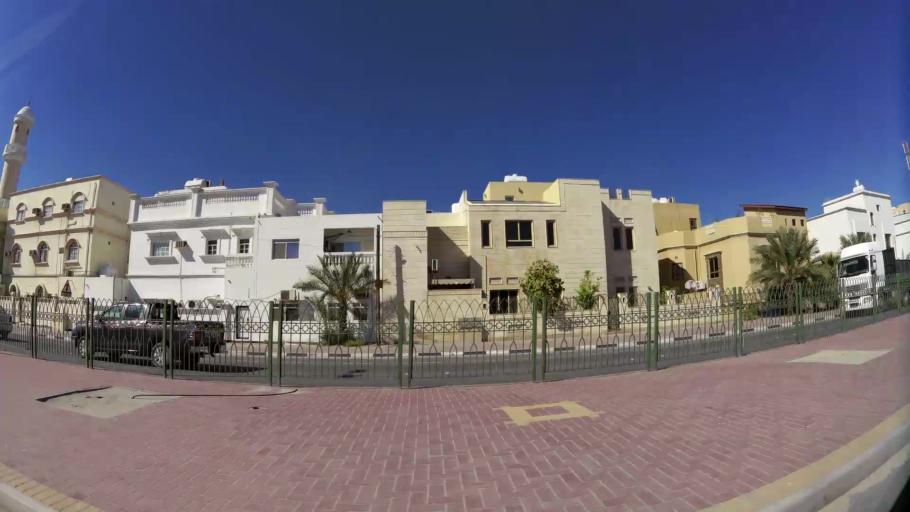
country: BH
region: Muharraq
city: Al Hadd
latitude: 26.2340
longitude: 50.6542
